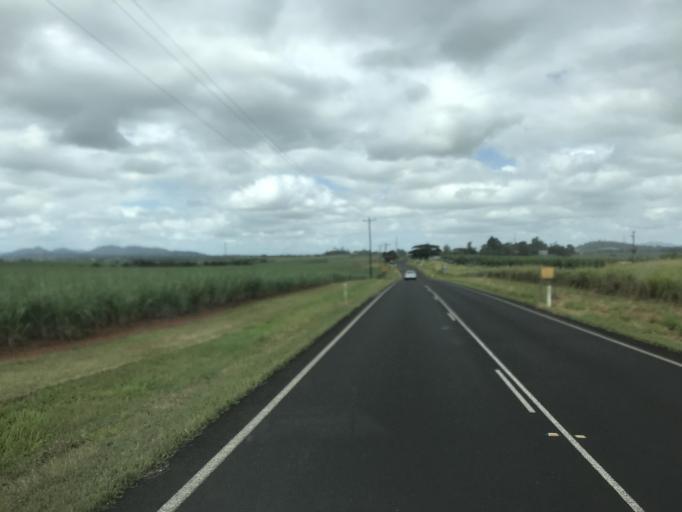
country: AU
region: Queensland
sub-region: Cassowary Coast
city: Innisfail
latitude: -17.5803
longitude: 145.9975
